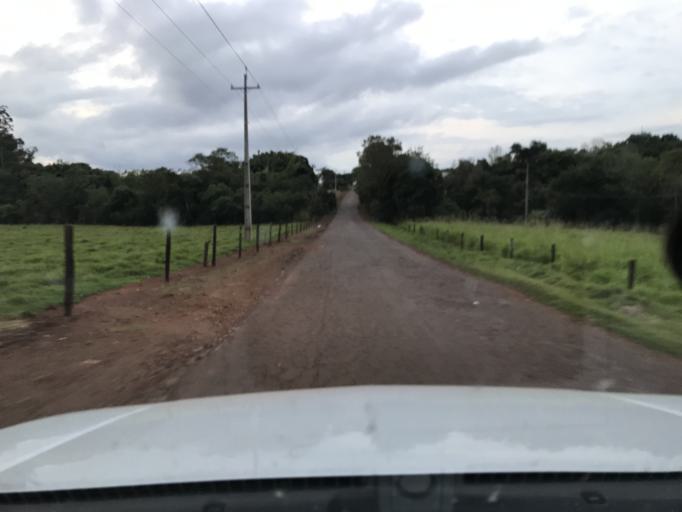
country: BR
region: Parana
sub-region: Palotina
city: Palotina
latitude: -24.2658
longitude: -53.8035
